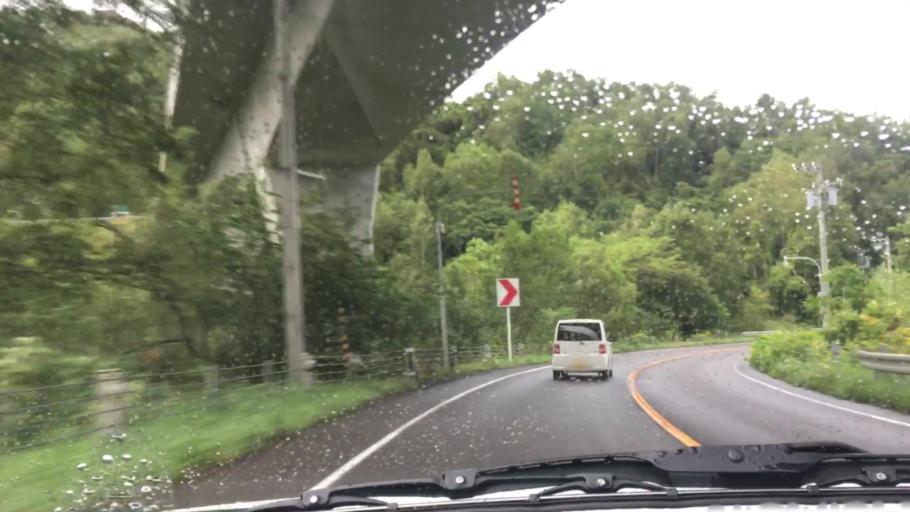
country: JP
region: Hokkaido
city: Date
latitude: 42.5834
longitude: 140.7272
